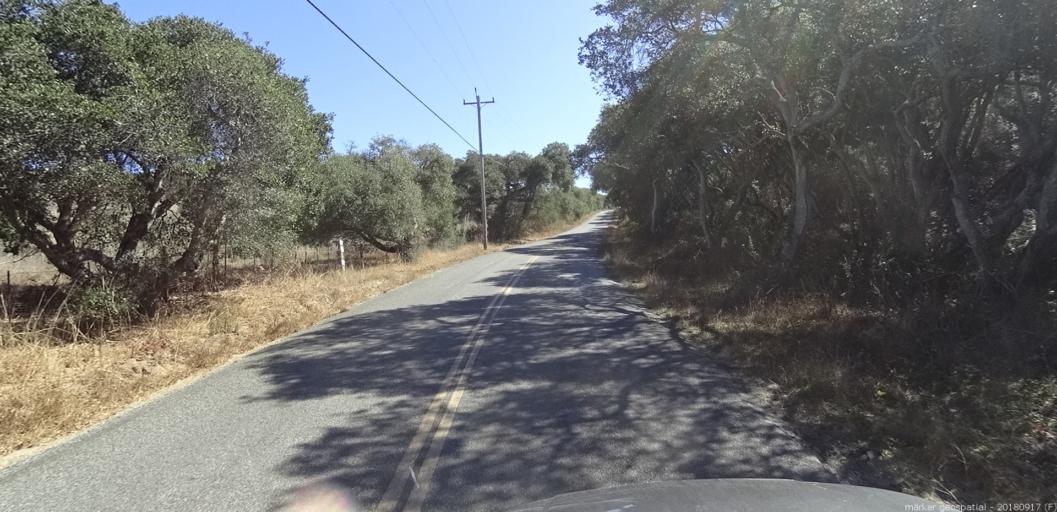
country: US
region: California
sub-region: Monterey County
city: Elkhorn
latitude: 36.8326
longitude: -121.6898
